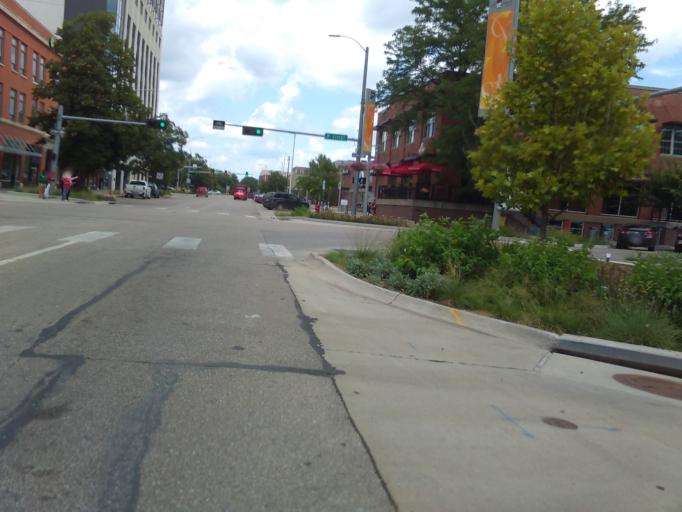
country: US
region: Nebraska
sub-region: Lancaster County
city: Lincoln
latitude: 40.8145
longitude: -96.7012
